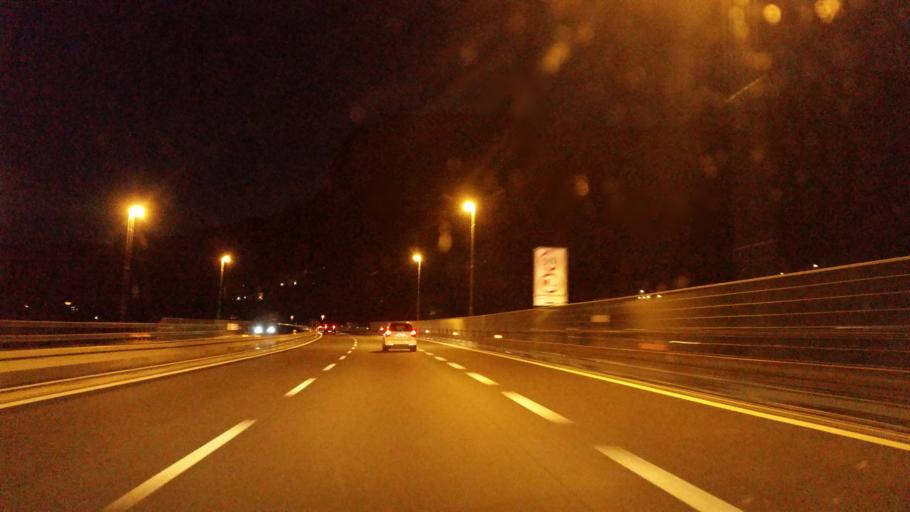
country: IT
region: Liguria
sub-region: Provincia di Savona
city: Calice Ligure
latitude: 44.1868
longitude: 8.3051
